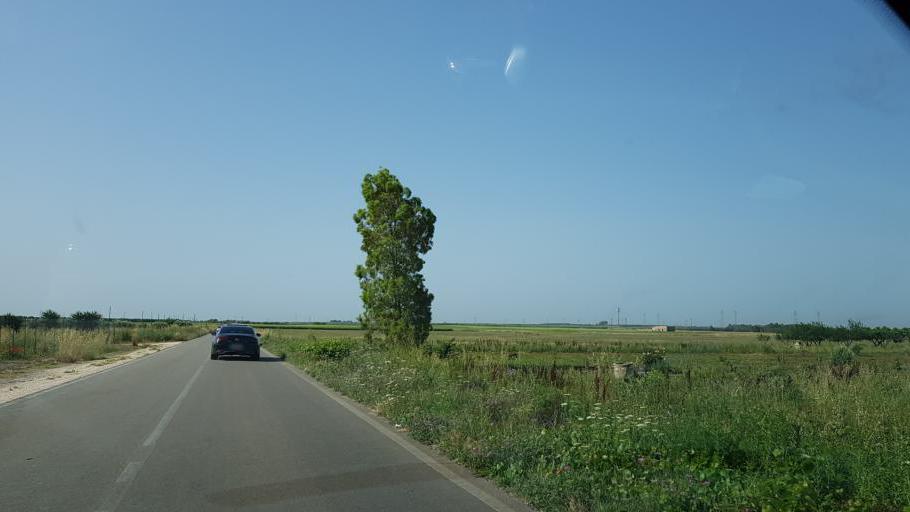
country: IT
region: Apulia
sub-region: Provincia di Brindisi
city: San Pancrazio Salentino
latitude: 40.3831
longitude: 17.8366
